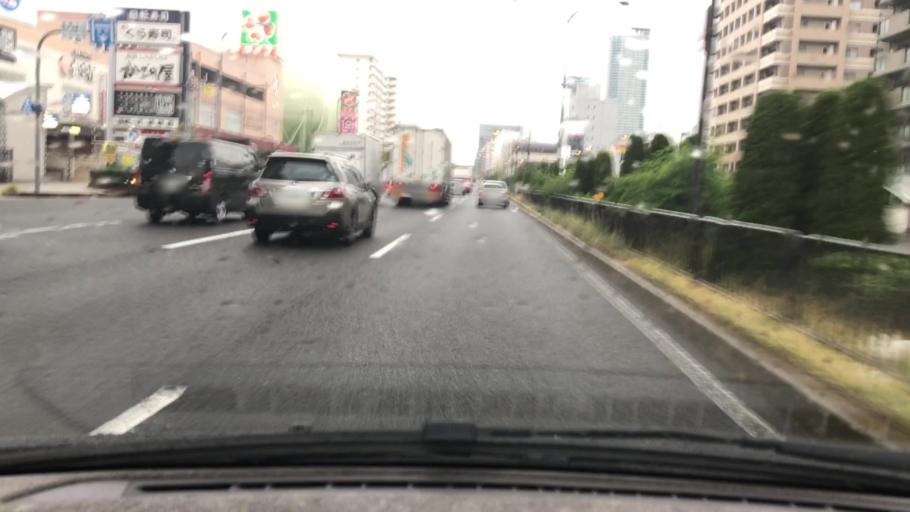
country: JP
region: Hyogo
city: Kobe
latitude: 34.6995
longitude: 135.2091
